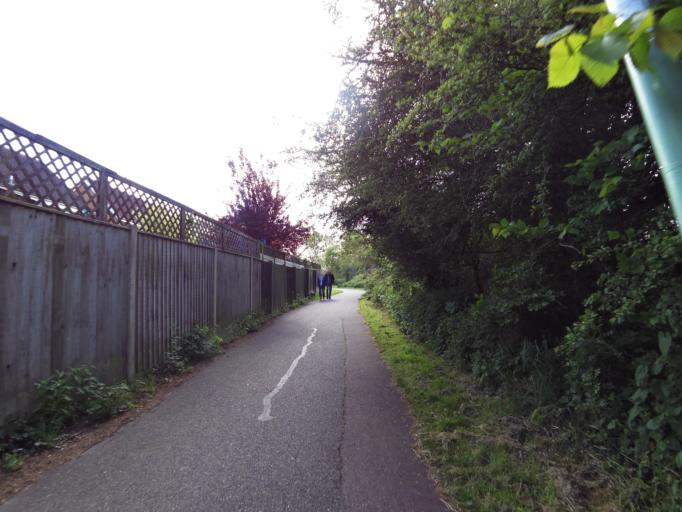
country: GB
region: England
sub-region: Suffolk
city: Beccles
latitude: 52.4497
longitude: 1.5920
